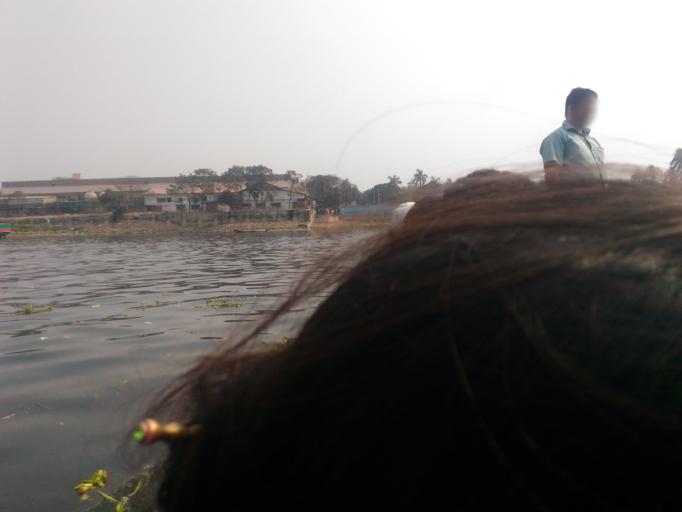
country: BD
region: Dhaka
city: Narayanganj
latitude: 23.6325
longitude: 90.4600
